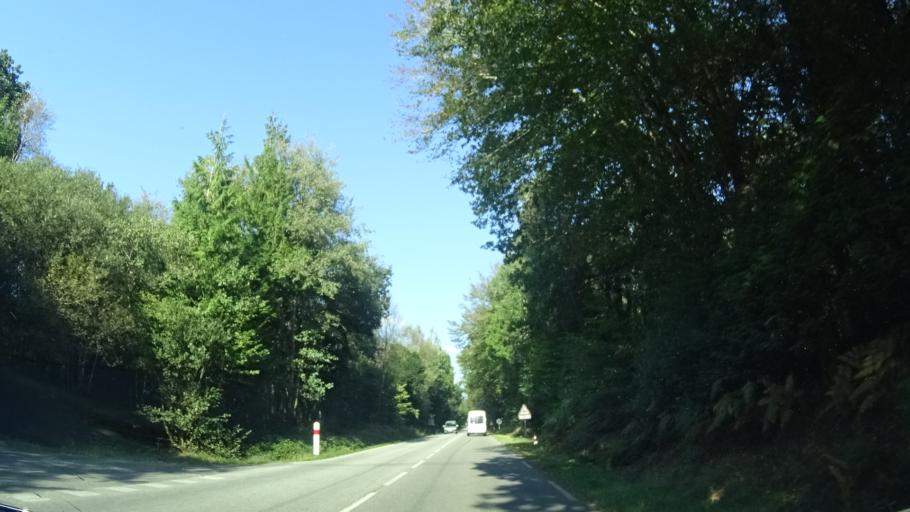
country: FR
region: Brittany
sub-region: Departement du Finistere
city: Cast
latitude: 48.1671
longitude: -4.1265
